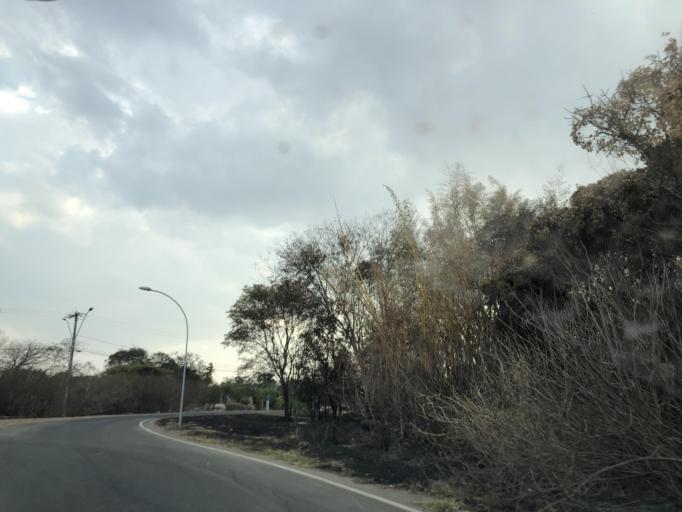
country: BR
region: Federal District
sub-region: Brasilia
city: Brasilia
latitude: -15.9383
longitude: -47.9751
